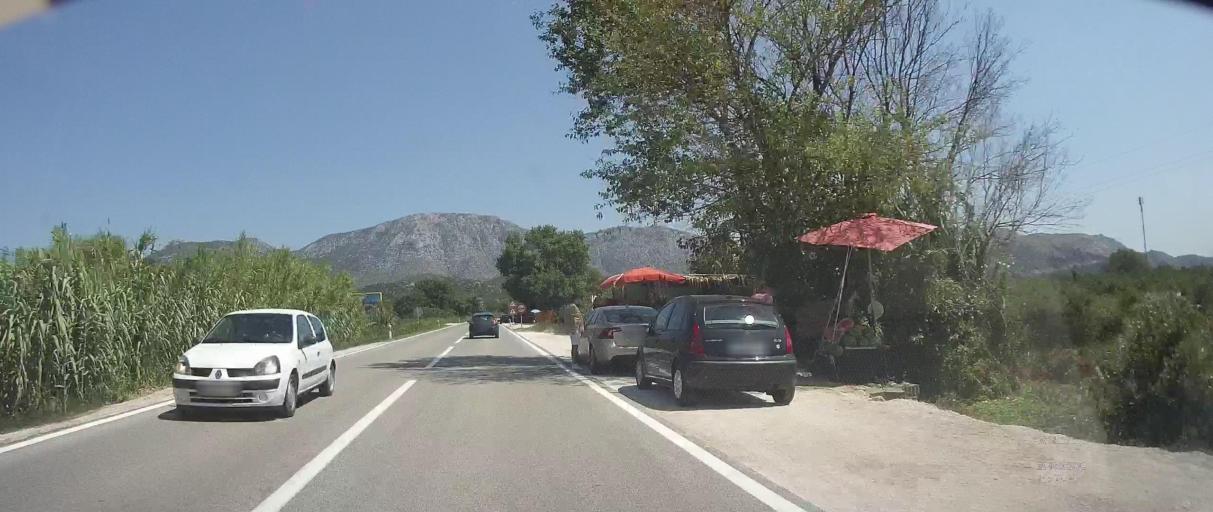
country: HR
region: Dubrovacko-Neretvanska
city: Komin
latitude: 43.0389
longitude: 17.4942
